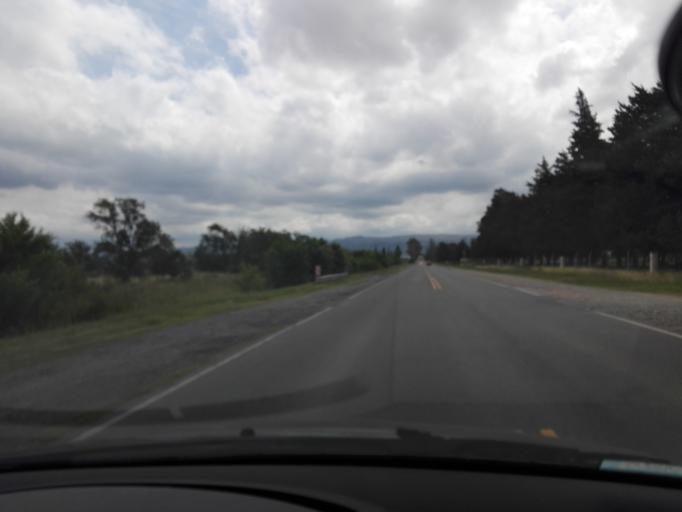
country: AR
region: Cordoba
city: Alta Gracia
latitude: -31.6582
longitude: -64.3978
